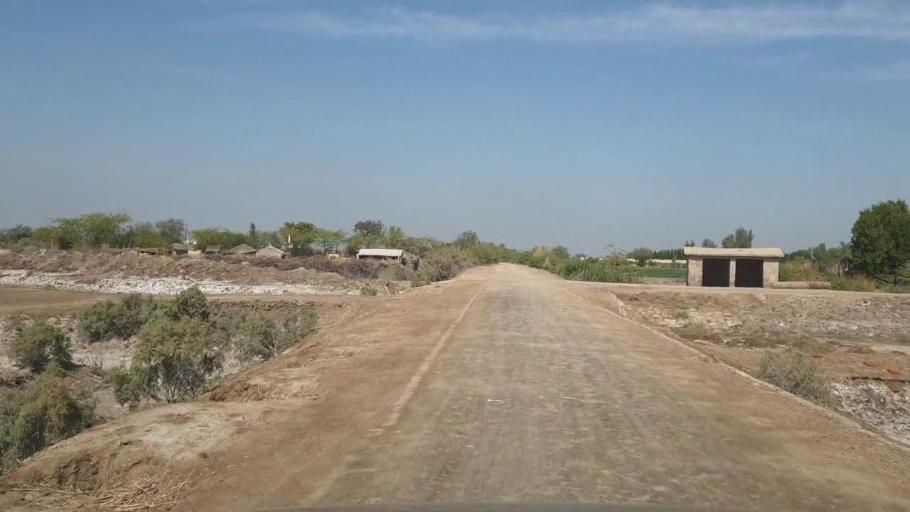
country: PK
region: Sindh
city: Mirwah Gorchani
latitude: 25.4304
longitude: 69.1865
